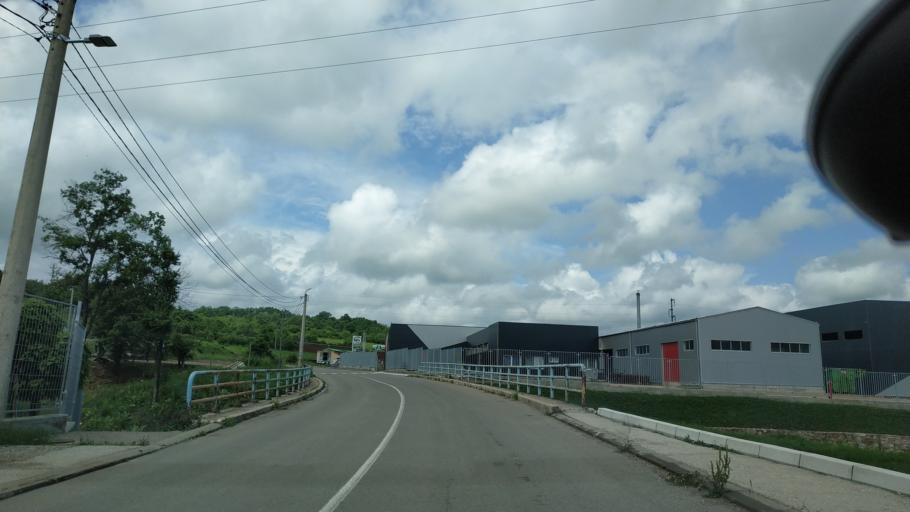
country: RS
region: Central Serbia
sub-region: Zajecarski Okrug
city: Boljevac
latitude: 43.8342
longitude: 21.9584
